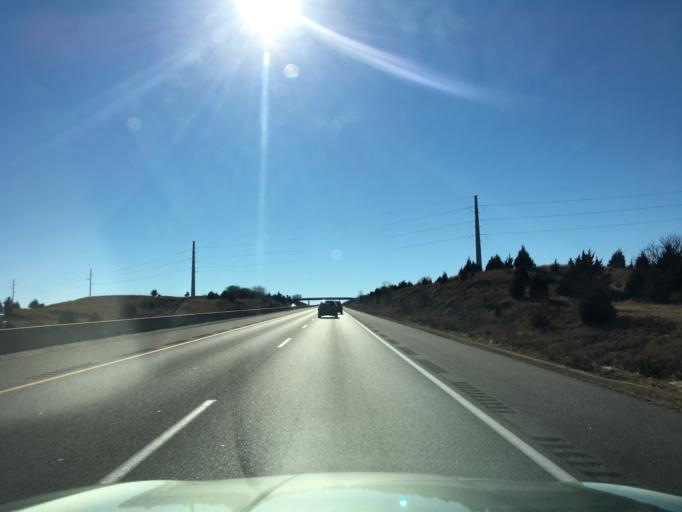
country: US
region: Kansas
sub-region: Sumner County
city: Wellington
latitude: 37.2081
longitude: -97.3400
